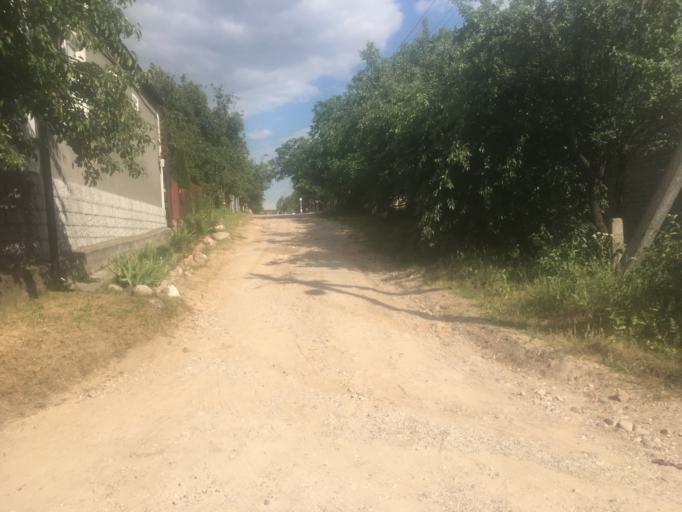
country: BY
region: Grodnenskaya
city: Hrodna
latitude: 53.6502
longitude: 23.8067
